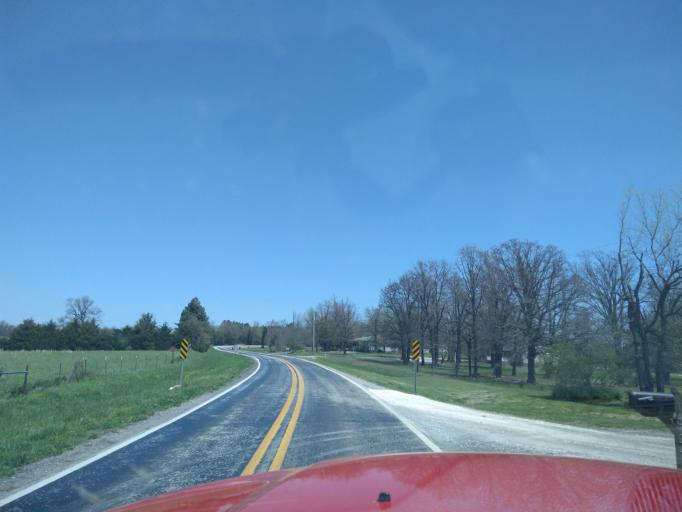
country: US
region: Arkansas
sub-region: Washington County
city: West Fork
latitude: 35.9020
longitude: -94.2354
